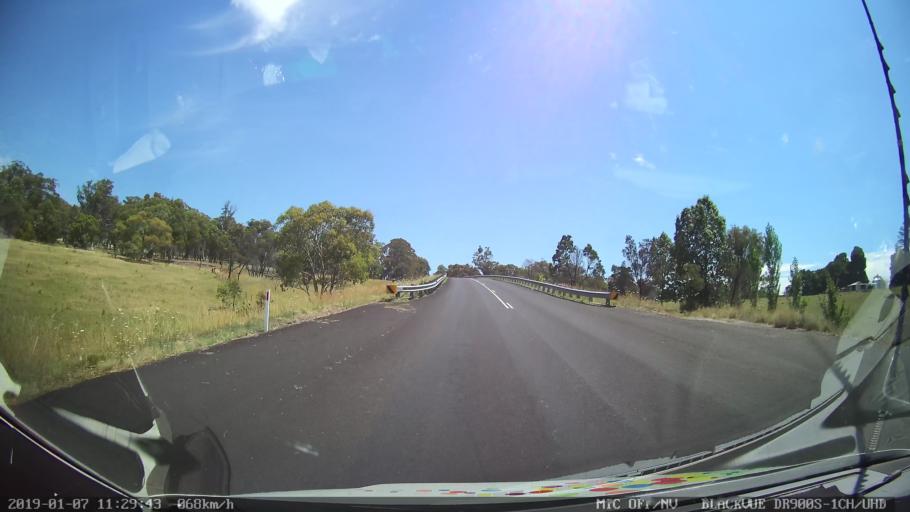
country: AU
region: New South Wales
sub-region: Armidale Dumaresq
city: Armidale
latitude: -30.4359
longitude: 151.5649
